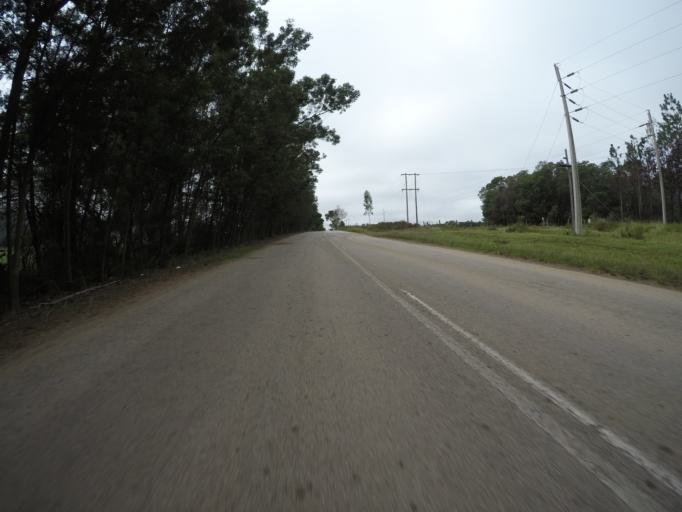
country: ZA
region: Eastern Cape
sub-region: Cacadu District Municipality
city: Kareedouw
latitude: -33.9966
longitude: 24.1454
